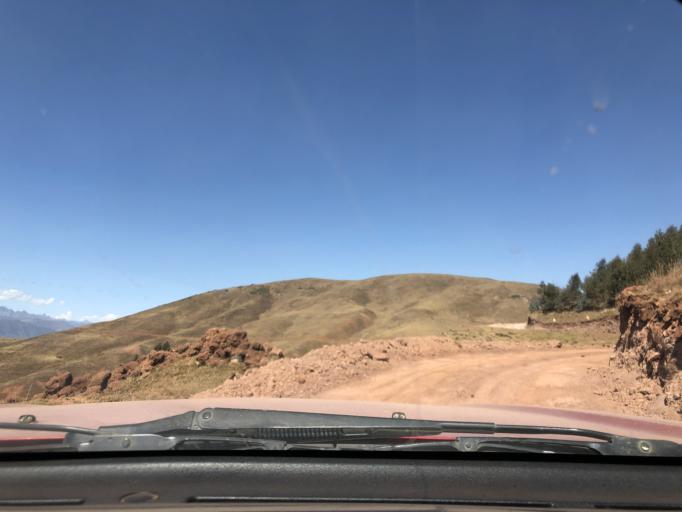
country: PE
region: Ayacucho
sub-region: Provincia de La Mar
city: Chilcas
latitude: -13.1811
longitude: -73.8407
